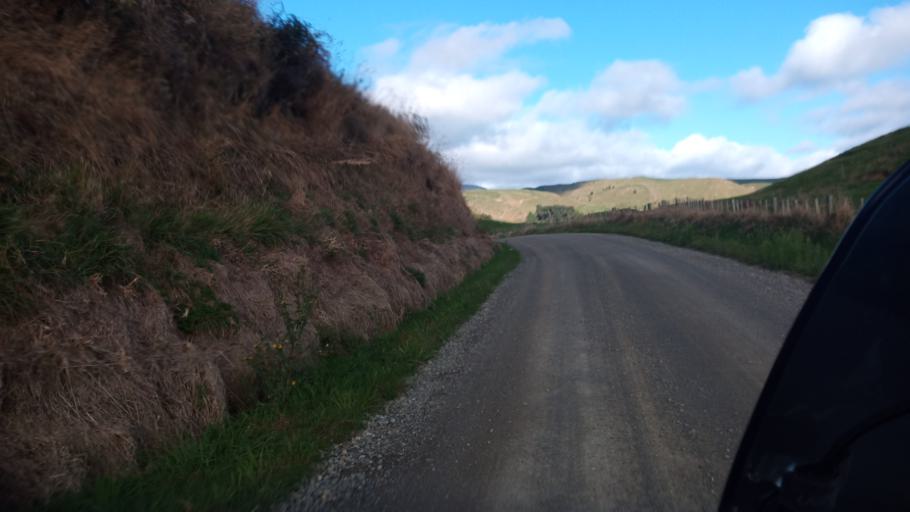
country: NZ
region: Bay of Plenty
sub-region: Opotiki District
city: Opotiki
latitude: -38.4554
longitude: 177.3935
